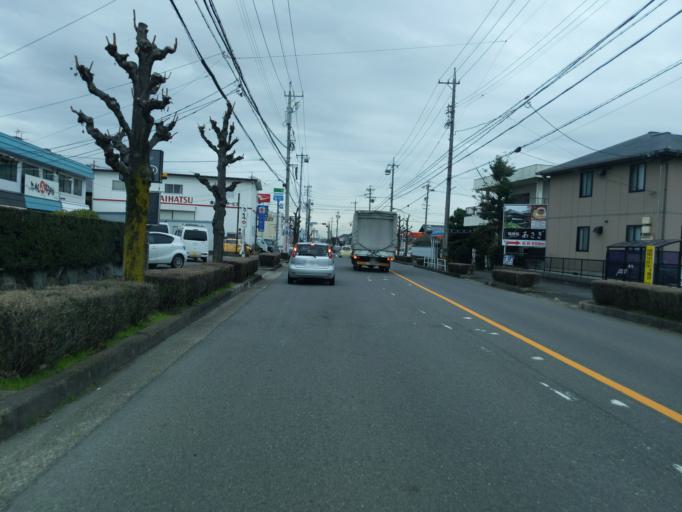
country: JP
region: Aichi
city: Kasugai
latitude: 35.2574
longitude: 136.9534
